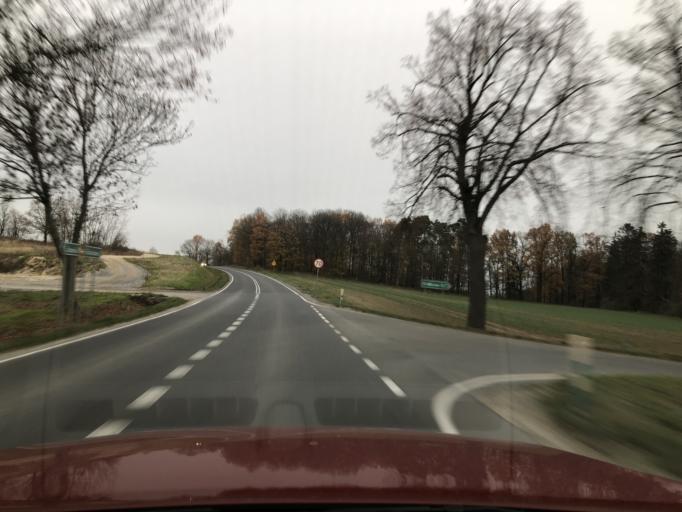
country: PL
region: Lower Silesian Voivodeship
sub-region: Powiat swidnicki
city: Zarow
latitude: 50.9715
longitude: 16.4979
